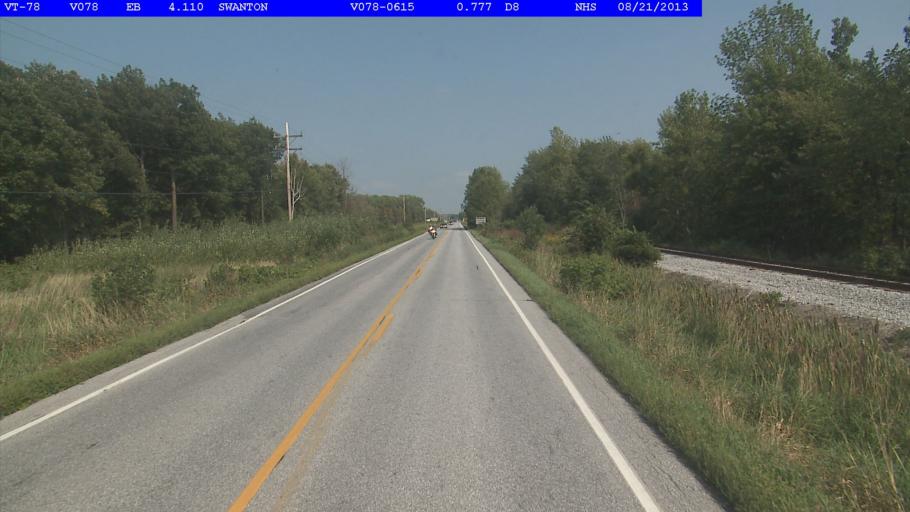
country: US
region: Vermont
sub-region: Franklin County
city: Swanton
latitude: 44.9695
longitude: -73.2055
